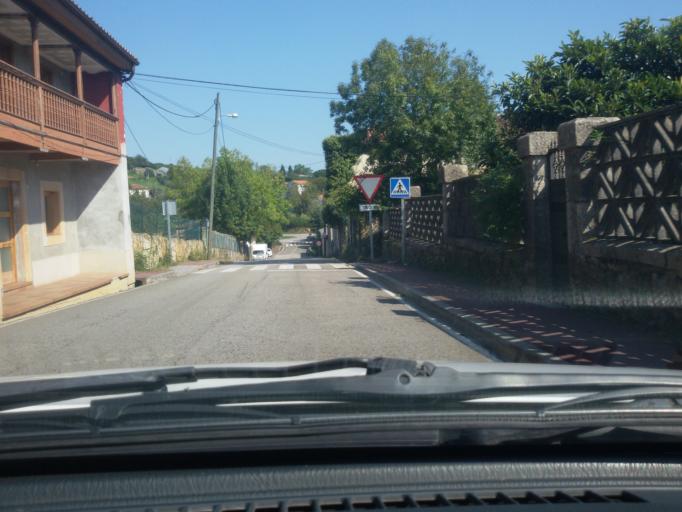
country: ES
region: Asturias
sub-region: Province of Asturias
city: Pola de Siero
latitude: 43.3913
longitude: -5.6714
